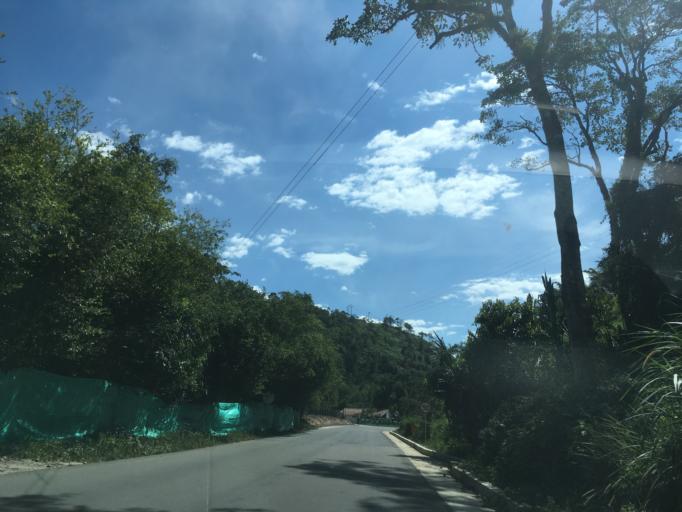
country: CO
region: Santander
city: Coromoro
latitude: 6.2941
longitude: -73.1461
